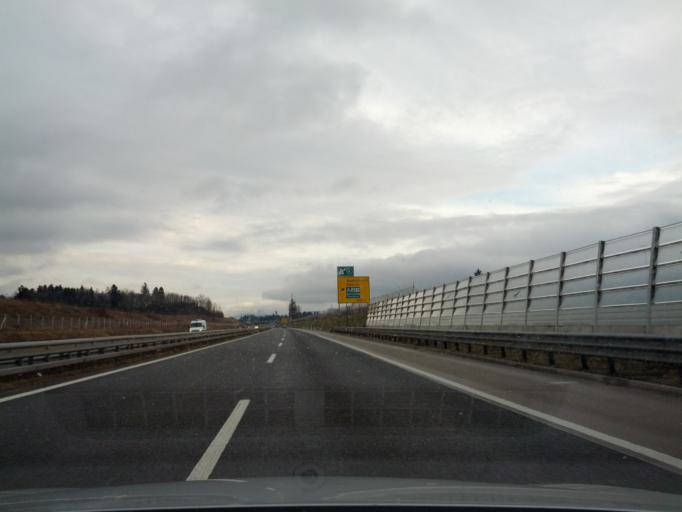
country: SI
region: Radovljica
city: Radovljica
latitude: 46.3481
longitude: 14.1804
